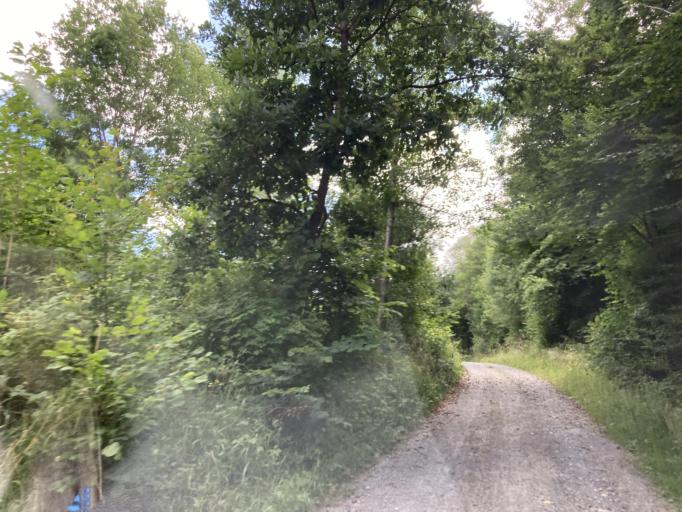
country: DE
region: Baden-Wuerttemberg
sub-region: Tuebingen Region
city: Ofterdingen
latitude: 48.4450
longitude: 9.0210
